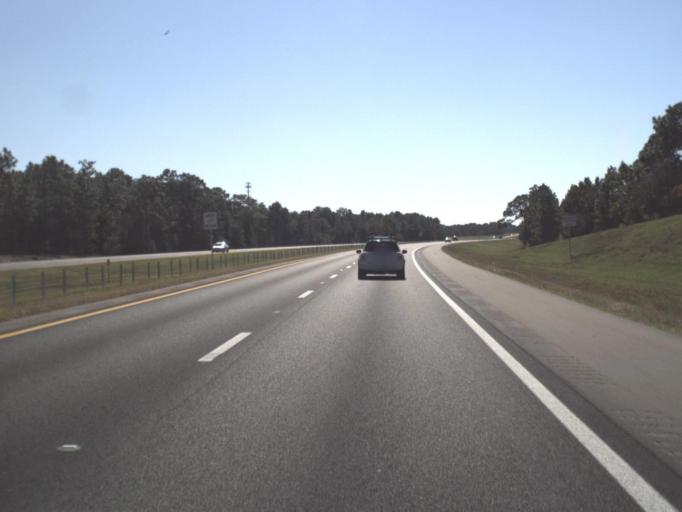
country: US
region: Florida
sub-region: Hernando County
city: Brookridge
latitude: 28.5163
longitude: -82.4774
